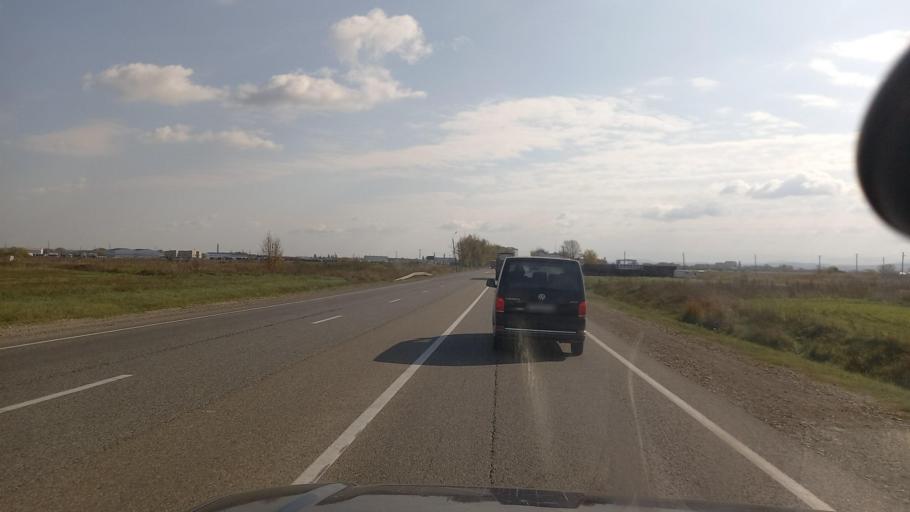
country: RU
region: Krasnodarskiy
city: Abinsk
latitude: 44.8726
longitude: 38.1212
